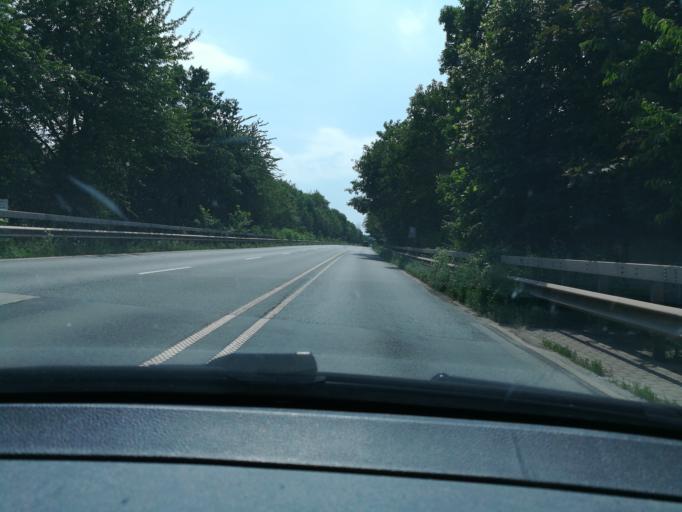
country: DE
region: North Rhine-Westphalia
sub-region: Regierungsbezirk Detmold
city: Minden
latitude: 52.2990
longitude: 8.9807
